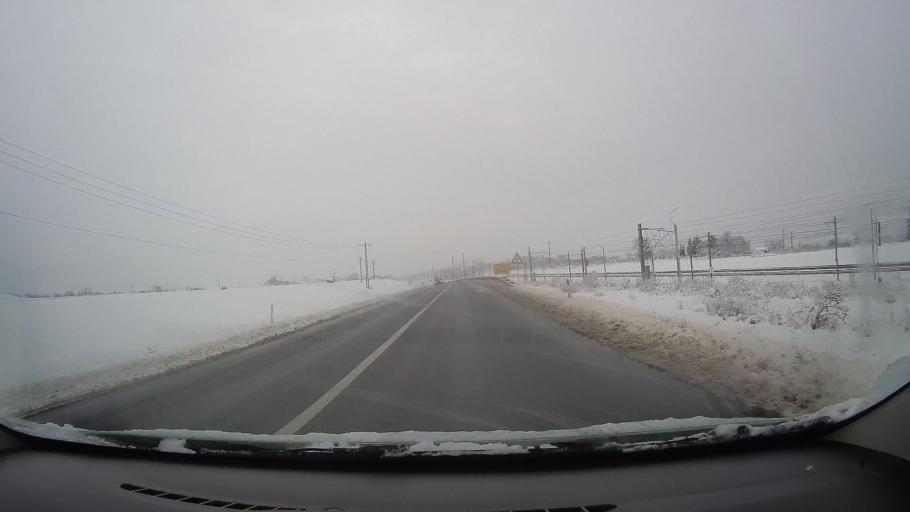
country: RO
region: Alba
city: Vurpar
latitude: 45.9868
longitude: 23.4926
